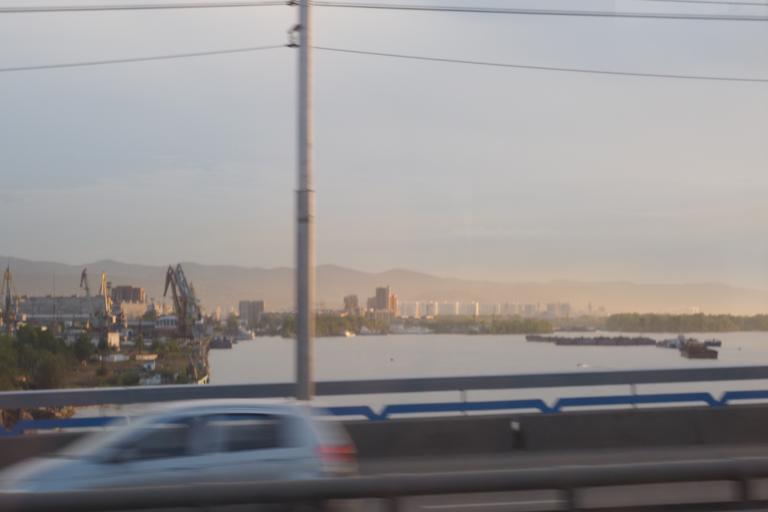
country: RU
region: Krasnoyarskiy
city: Krasnoyarsk
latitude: 56.0177
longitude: 92.9536
